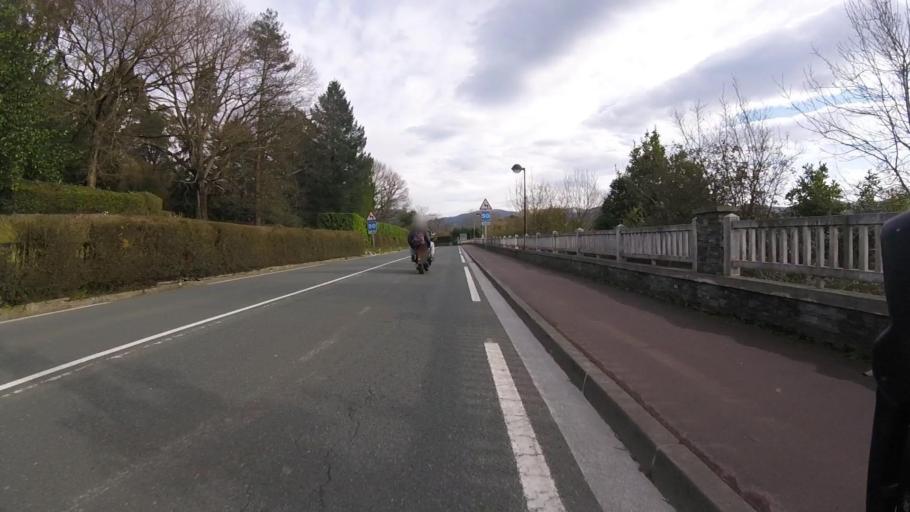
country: ES
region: Basque Country
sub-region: Provincia de Guipuzcoa
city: Lezo
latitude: 43.3026
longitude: -1.8722
